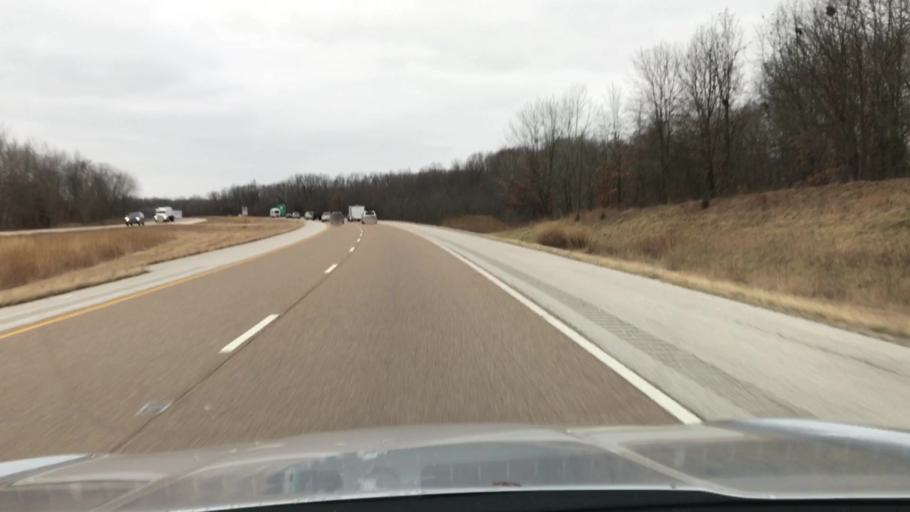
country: US
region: Illinois
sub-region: Macoupin County
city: Mount Olive
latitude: 39.0851
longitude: -89.7523
